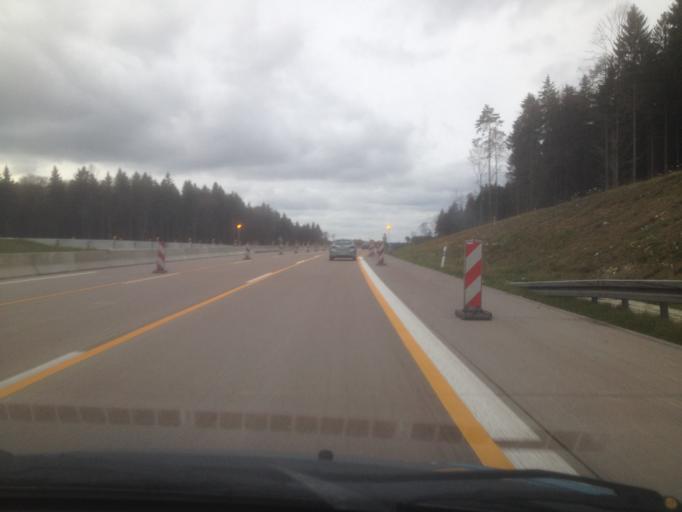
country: DE
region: Bavaria
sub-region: Swabia
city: Horgau
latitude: 48.4132
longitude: 10.6584
